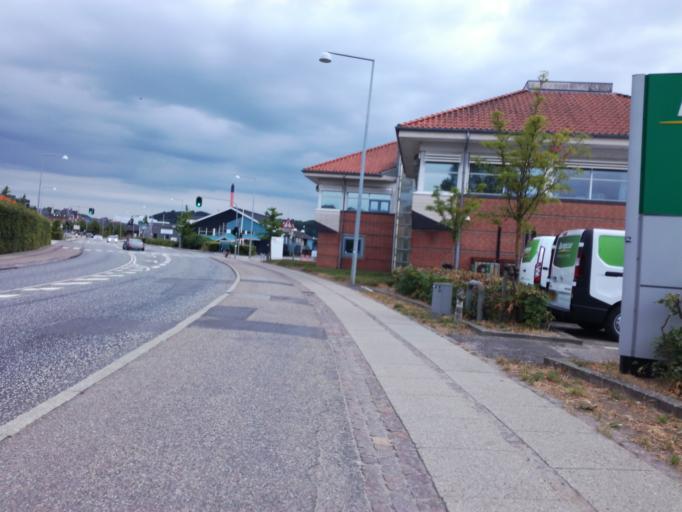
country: DK
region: South Denmark
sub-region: Vejle Kommune
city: Vejle
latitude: 55.7036
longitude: 9.5438
